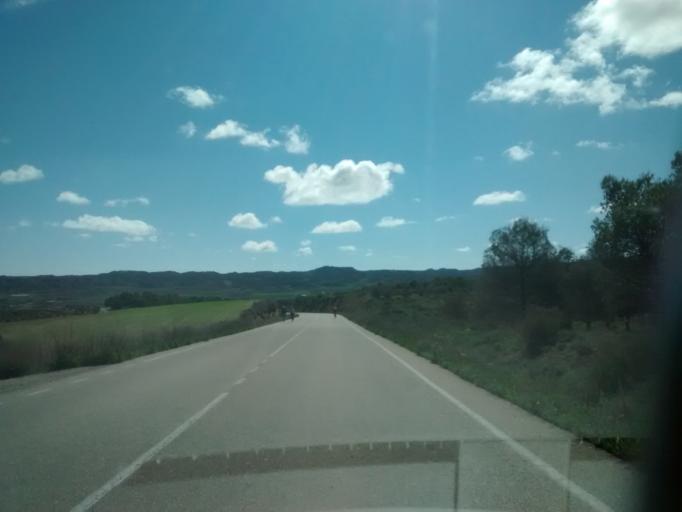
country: ES
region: Aragon
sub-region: Provincia de Zaragoza
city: Lecinena
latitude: 41.7904
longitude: -0.6306
